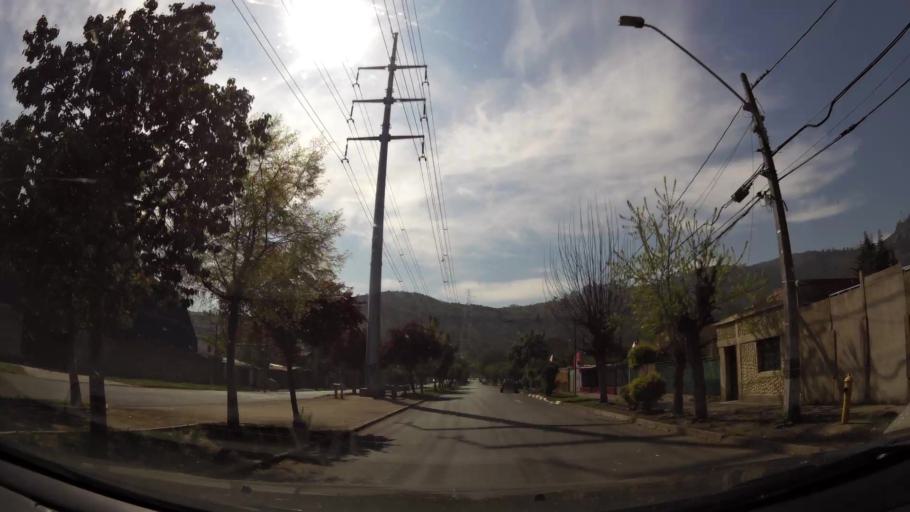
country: CL
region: Santiago Metropolitan
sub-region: Provincia de Santiago
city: Santiago
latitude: -33.4008
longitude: -70.6229
